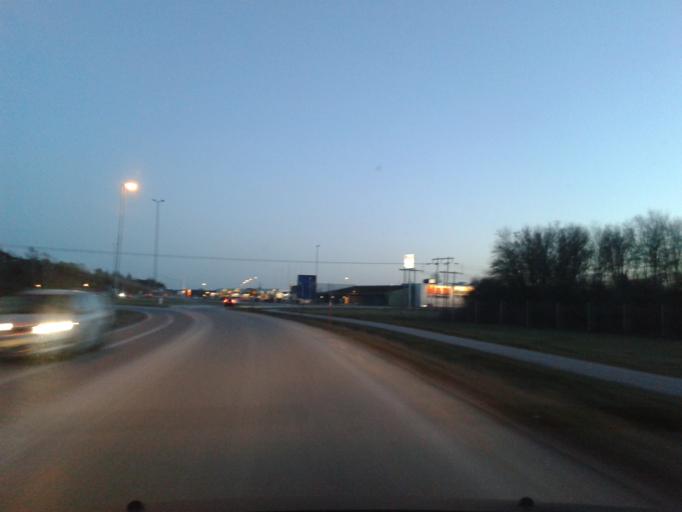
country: SE
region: Gotland
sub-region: Gotland
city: Visby
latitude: 57.6260
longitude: 18.3192
